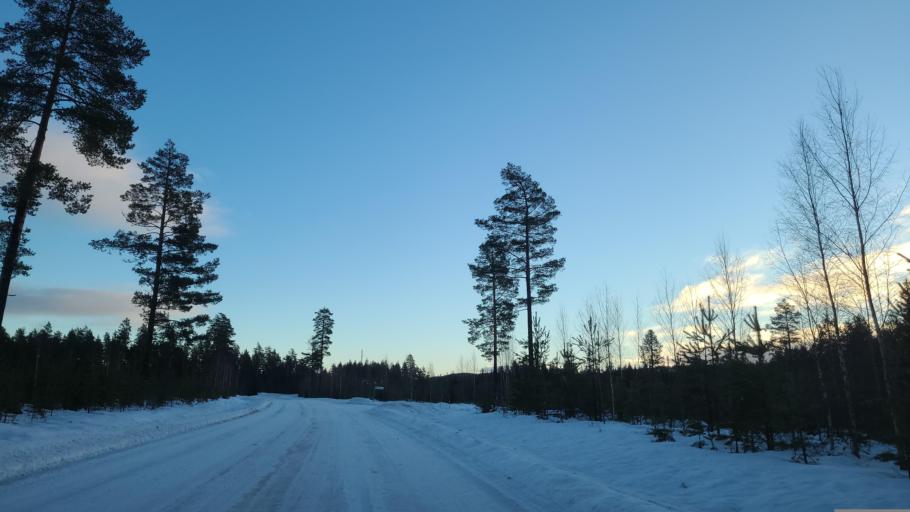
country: SE
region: Gaevleborg
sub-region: Bollnas Kommun
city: Kilafors
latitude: 61.3603
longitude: 16.6696
